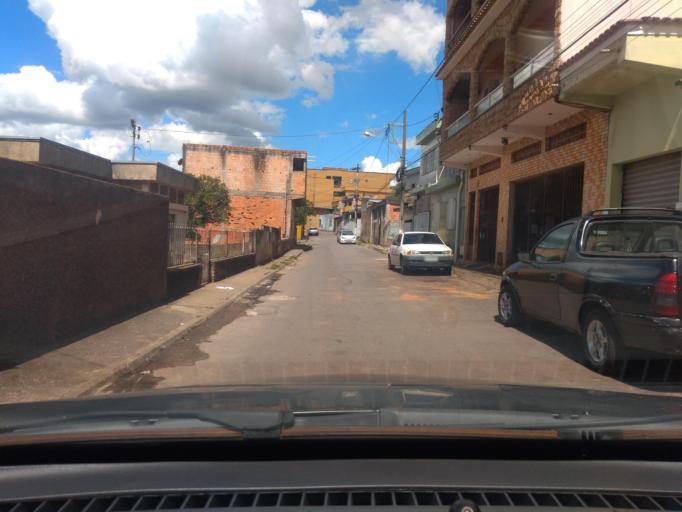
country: BR
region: Minas Gerais
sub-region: Tres Coracoes
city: Tres Coracoes
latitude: -21.6925
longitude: -45.2436
